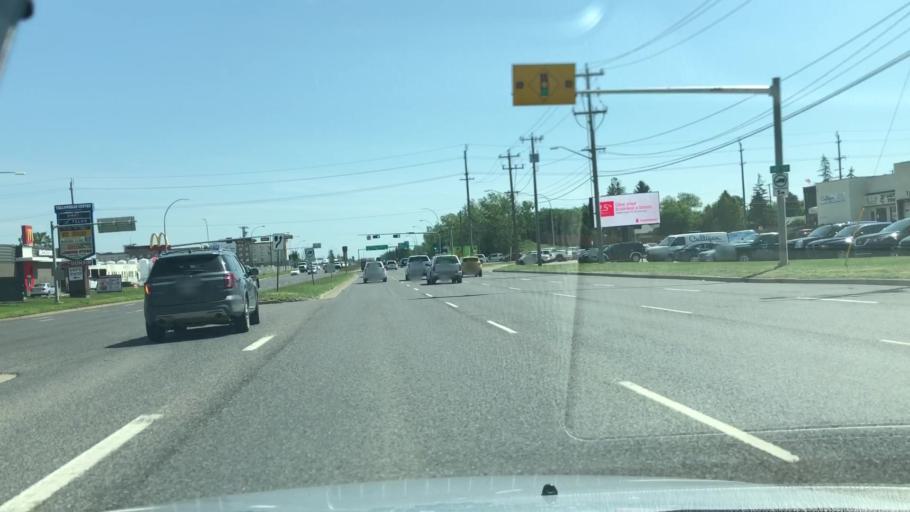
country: CA
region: Alberta
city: St. Albert
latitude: 53.5811
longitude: -113.5679
